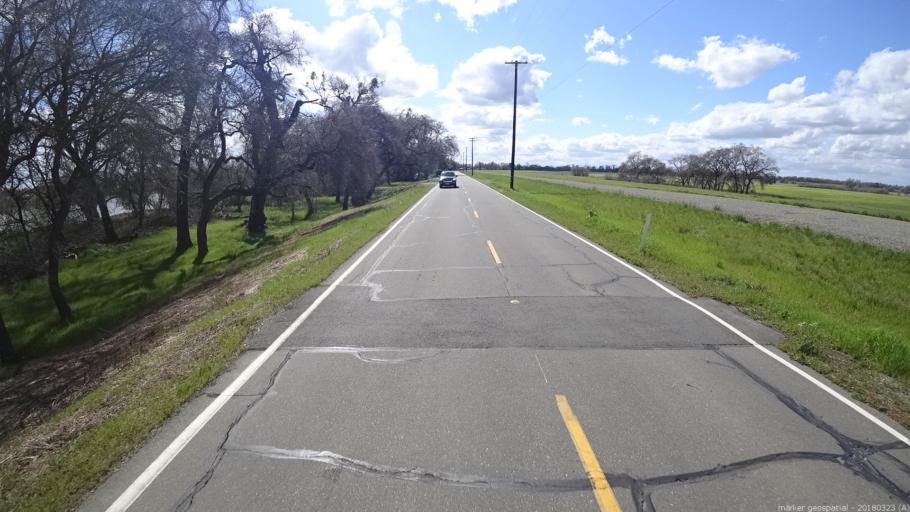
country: US
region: California
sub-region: Yolo County
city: West Sacramento
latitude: 38.6486
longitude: -121.5797
